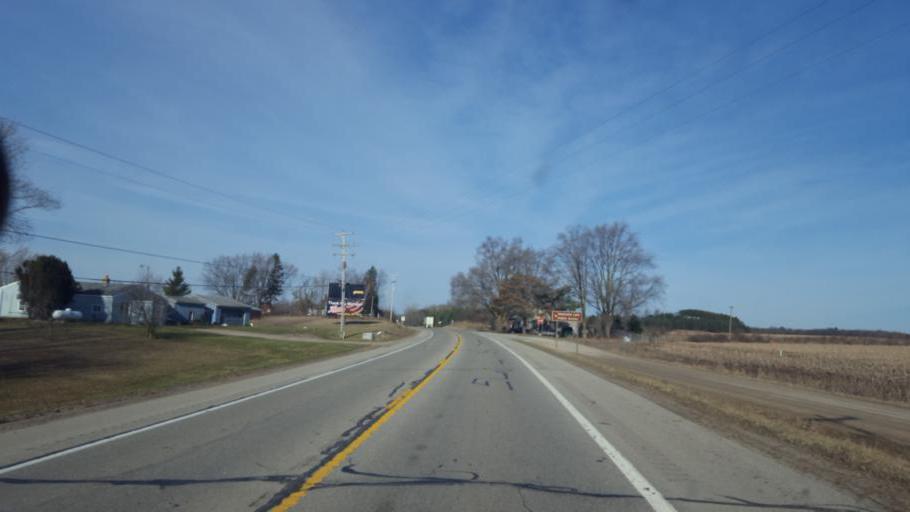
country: US
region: Michigan
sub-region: Montcalm County
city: Lakeview
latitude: 43.4299
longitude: -85.1613
